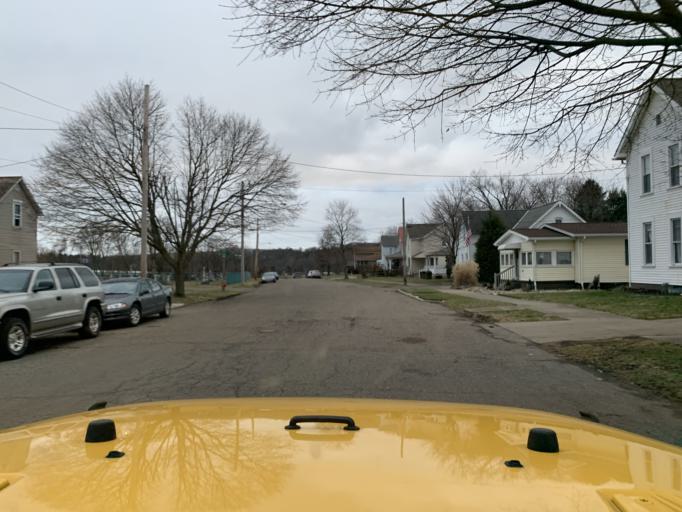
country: US
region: Ohio
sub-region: Tuscarawas County
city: Dover
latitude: 40.5226
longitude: -81.4849
